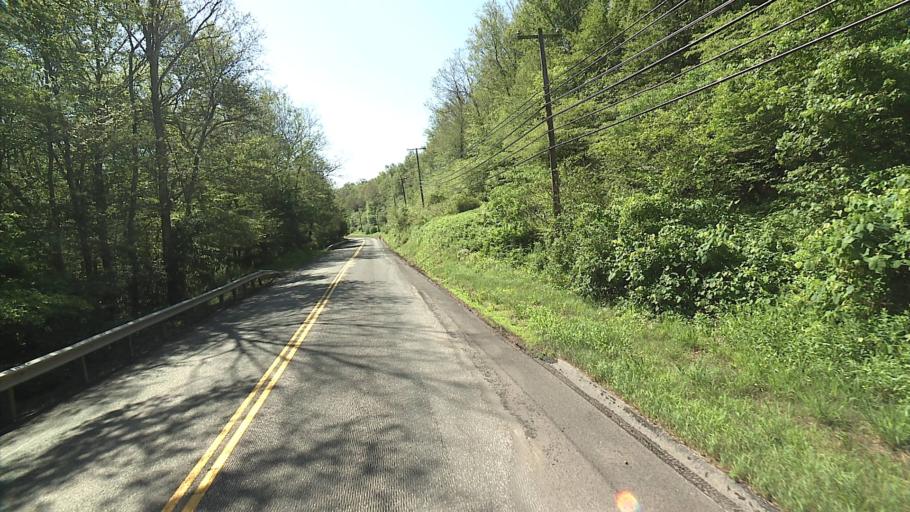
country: US
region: Connecticut
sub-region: Middlesex County
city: East Hampton
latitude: 41.5629
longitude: -72.4623
